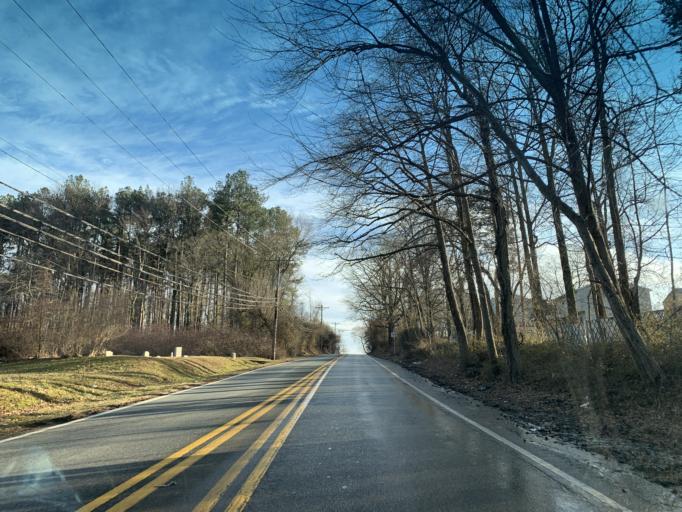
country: US
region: Delaware
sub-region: New Castle County
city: Bear
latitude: 39.6705
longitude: -75.6586
